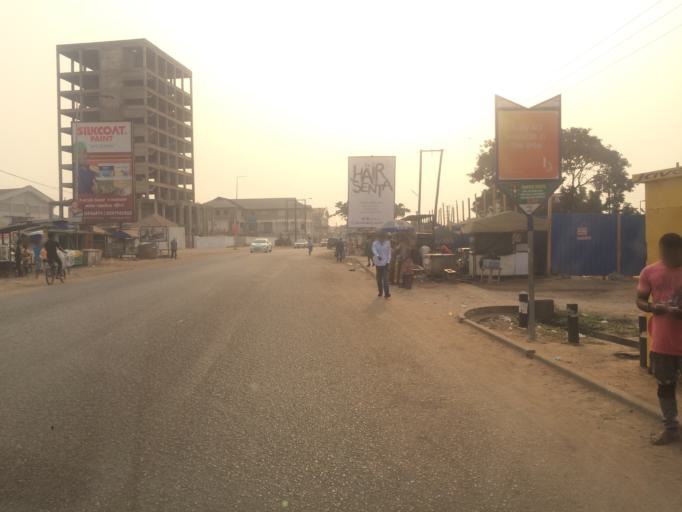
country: GH
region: Greater Accra
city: Nungua
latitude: 5.6249
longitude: -0.0759
